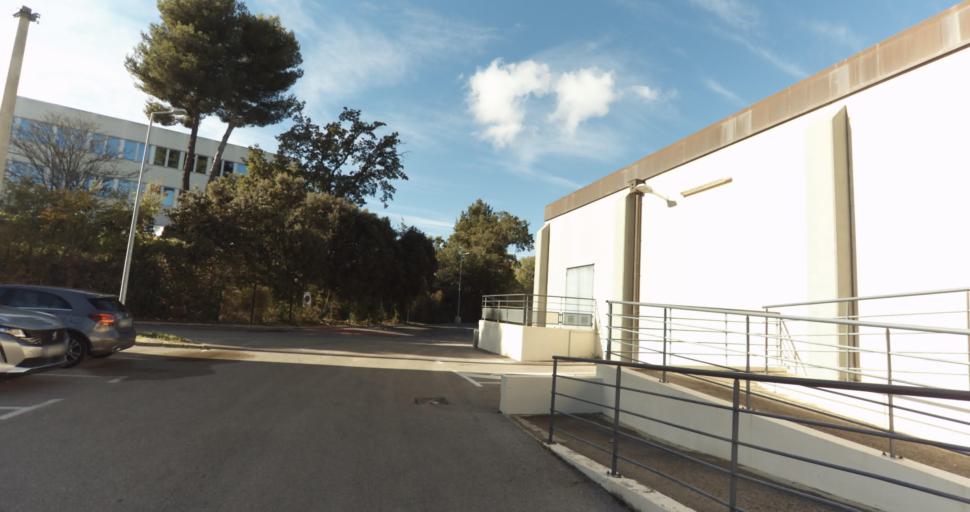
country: FR
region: Provence-Alpes-Cote d'Azur
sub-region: Departement des Bouches-du-Rhone
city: Venelles
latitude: 43.5842
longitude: 5.4731
